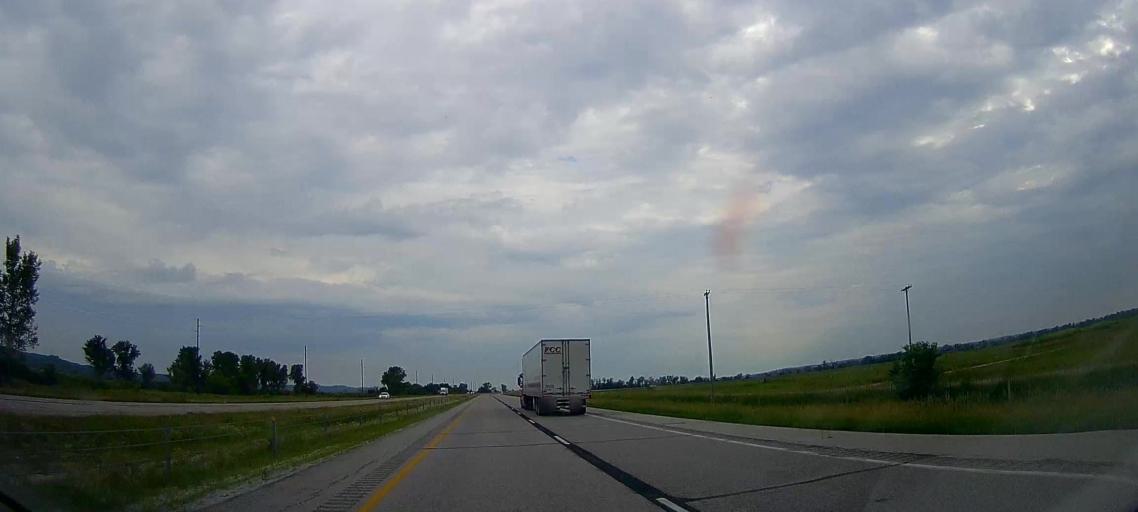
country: US
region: Iowa
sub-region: Harrison County
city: Missouri Valley
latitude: 41.4775
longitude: -95.9000
